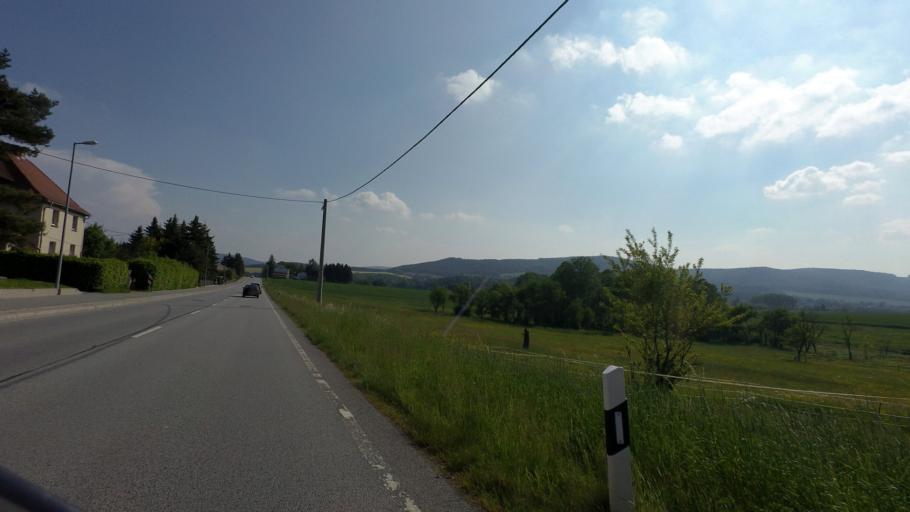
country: DE
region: Saxony
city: Grosspostwitz
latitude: 51.1303
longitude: 14.4412
